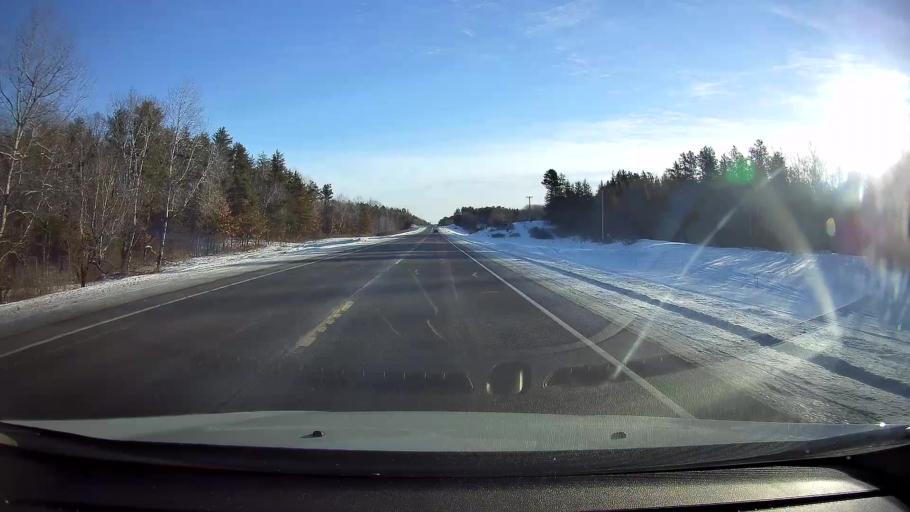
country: US
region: Wisconsin
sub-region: Washburn County
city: Spooner
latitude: 45.9104
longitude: -91.7941
